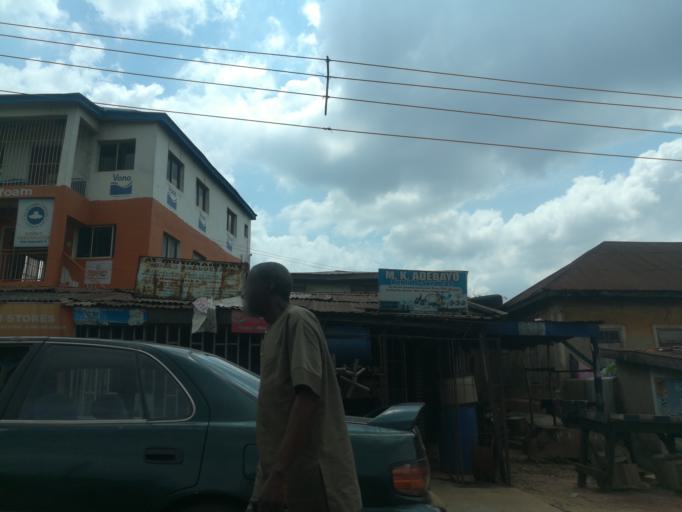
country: NG
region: Oyo
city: Ibadan
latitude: 7.3931
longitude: 3.9155
